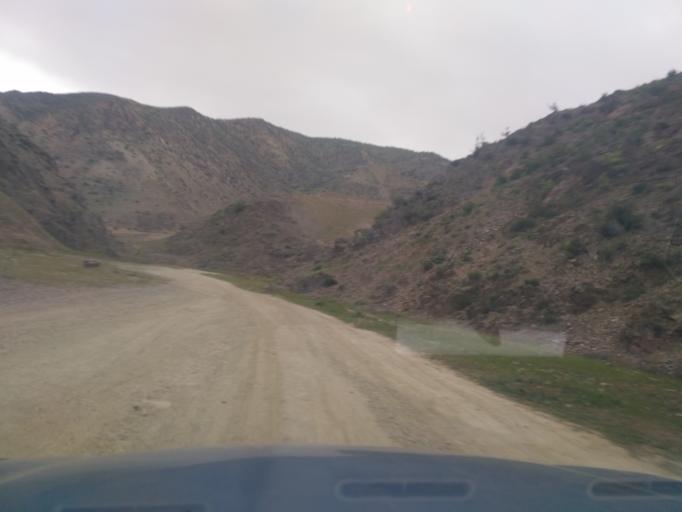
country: UZ
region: Jizzax
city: Zomin
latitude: 39.8552
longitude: 68.3894
